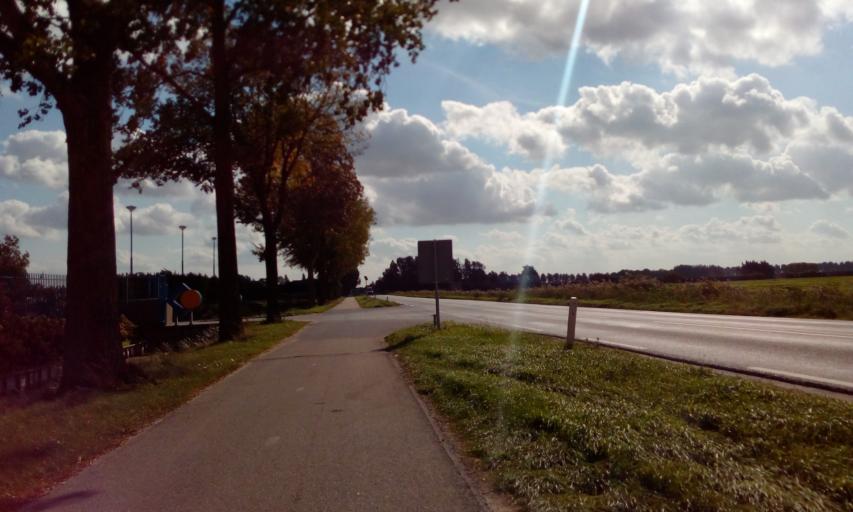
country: NL
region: South Holland
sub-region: Gemeente Waddinxveen
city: Waddinxveen
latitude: 52.0065
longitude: 4.6383
